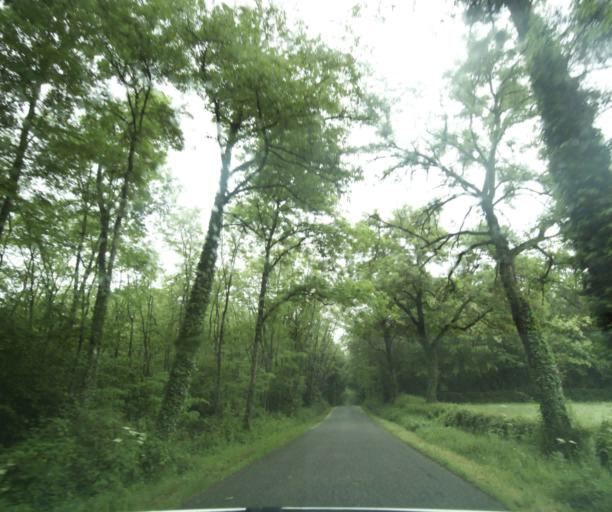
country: FR
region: Bourgogne
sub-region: Departement de Saone-et-Loire
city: Charolles
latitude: 46.4175
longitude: 4.1971
